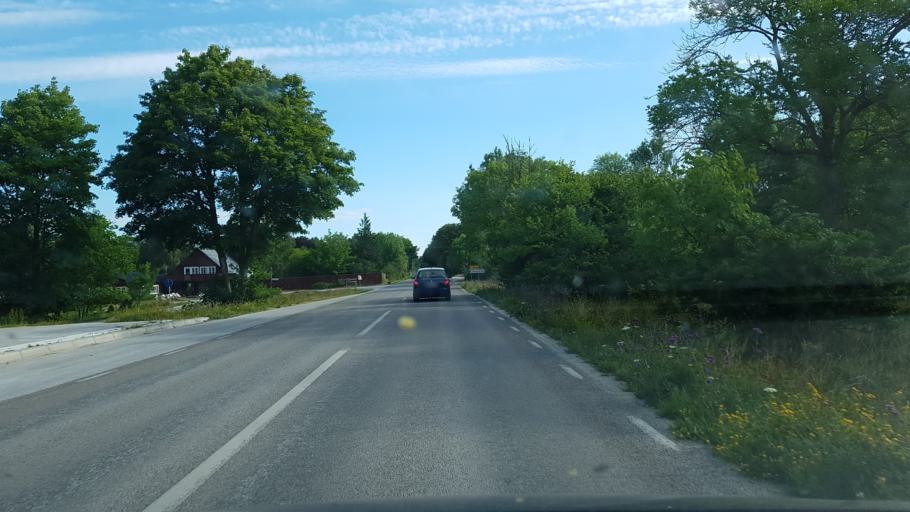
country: SE
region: Gotland
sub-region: Gotland
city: Visby
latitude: 57.7494
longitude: 18.4212
